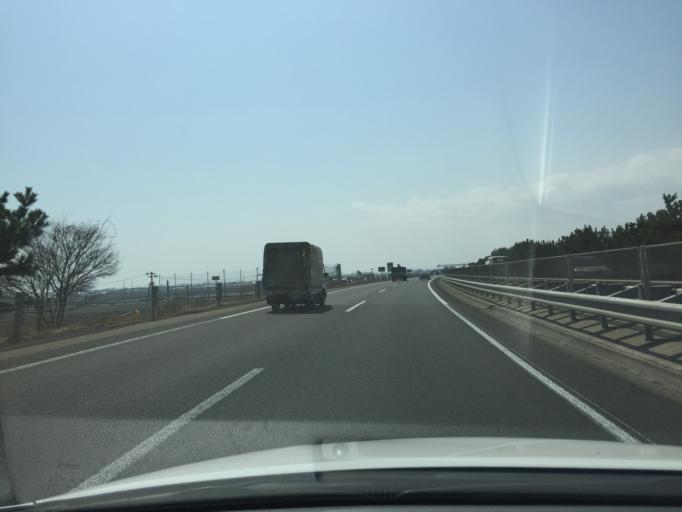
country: JP
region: Miyagi
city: Sendai-shi
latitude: 38.2295
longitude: 140.9536
